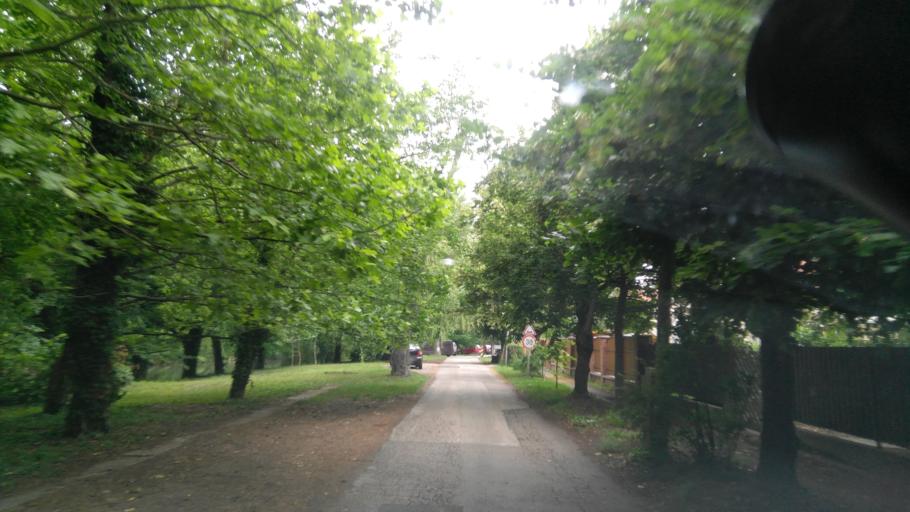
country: HU
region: Bekes
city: Bekescsaba
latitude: 46.6892
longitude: 21.0969
